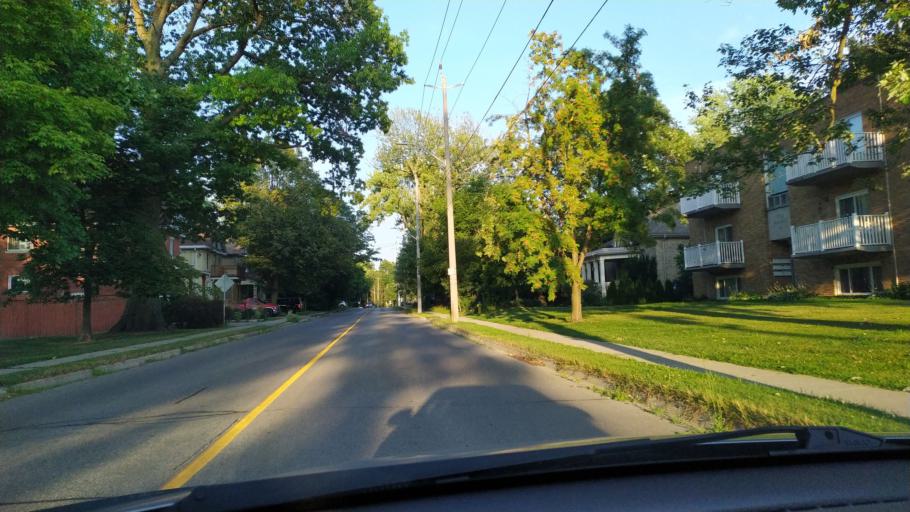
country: CA
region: Ontario
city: Stratford
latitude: 43.3626
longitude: -80.9804
